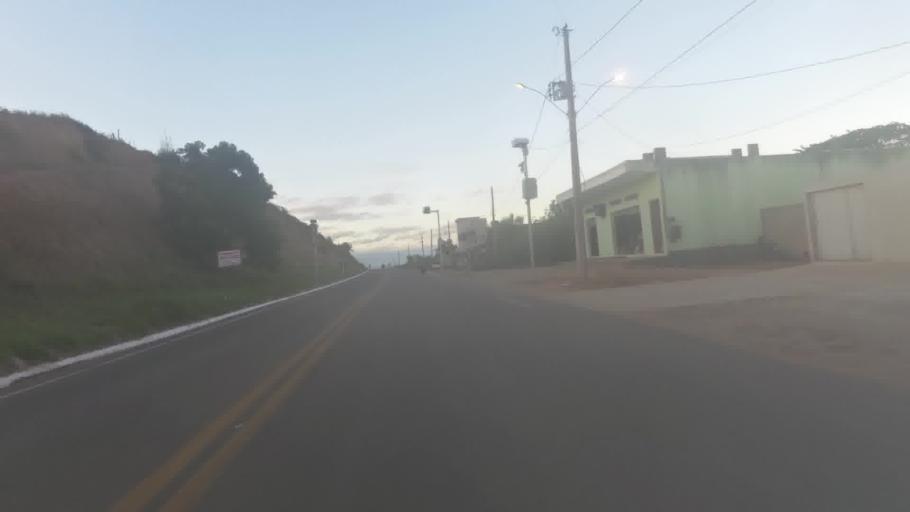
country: BR
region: Espirito Santo
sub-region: Marataizes
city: Marataizes
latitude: -21.1126
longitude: -40.8562
